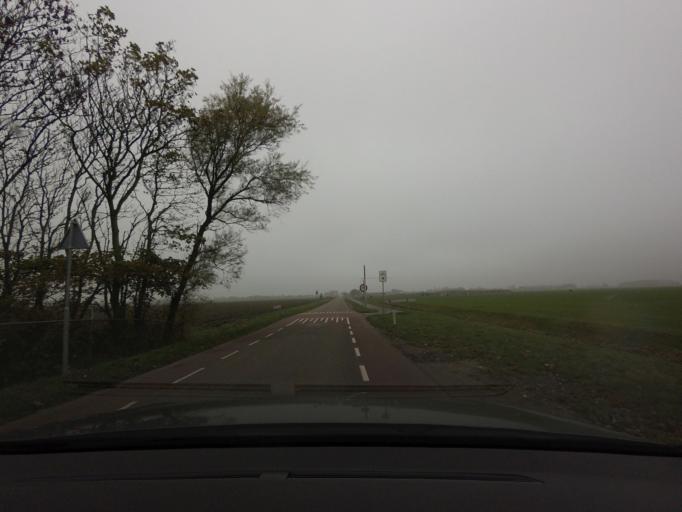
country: NL
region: North Holland
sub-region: Gemeente Schagen
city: Harenkarspel
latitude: 52.7438
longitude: 4.7157
